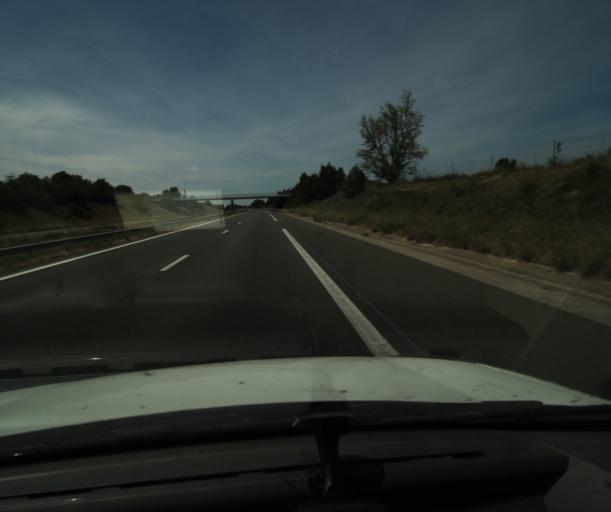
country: FR
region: Languedoc-Roussillon
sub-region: Departement de l'Aude
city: Trebes
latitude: 43.1883
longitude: 2.4653
